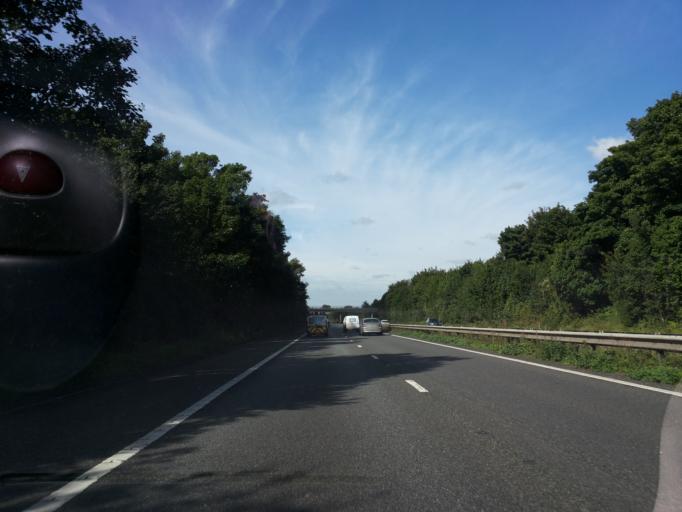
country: GB
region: England
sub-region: Kent
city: Sittingbourne
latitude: 51.3148
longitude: 0.7017
